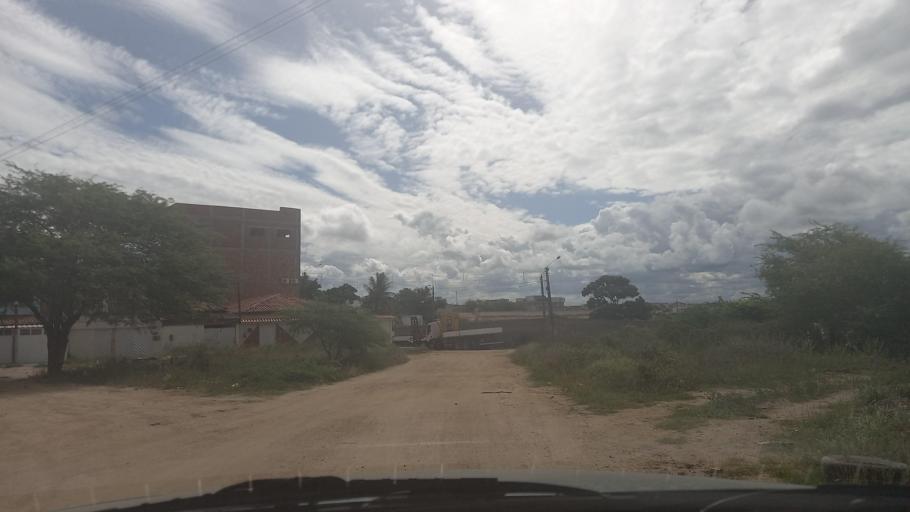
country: BR
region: Pernambuco
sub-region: Caruaru
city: Caruaru
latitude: -8.2904
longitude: -35.9916
